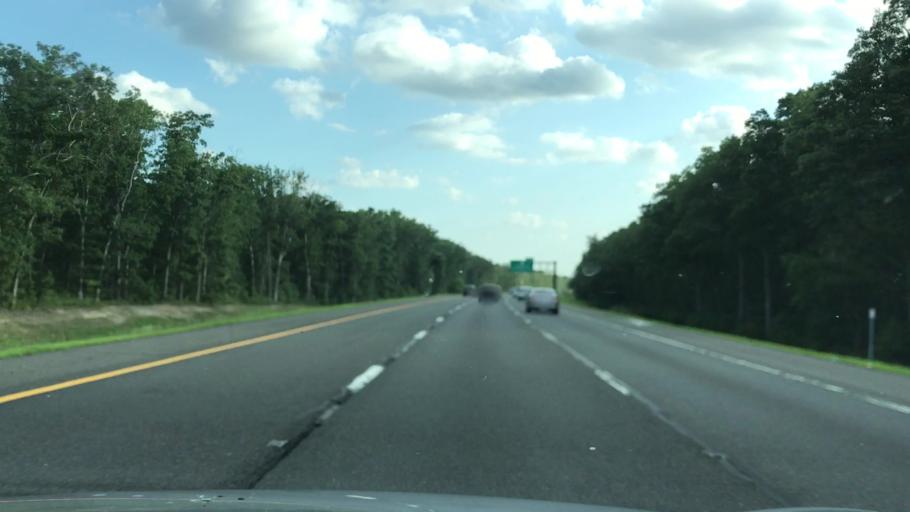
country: US
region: New Jersey
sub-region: Ocean County
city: Ocean Acres
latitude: 39.7396
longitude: -74.2595
